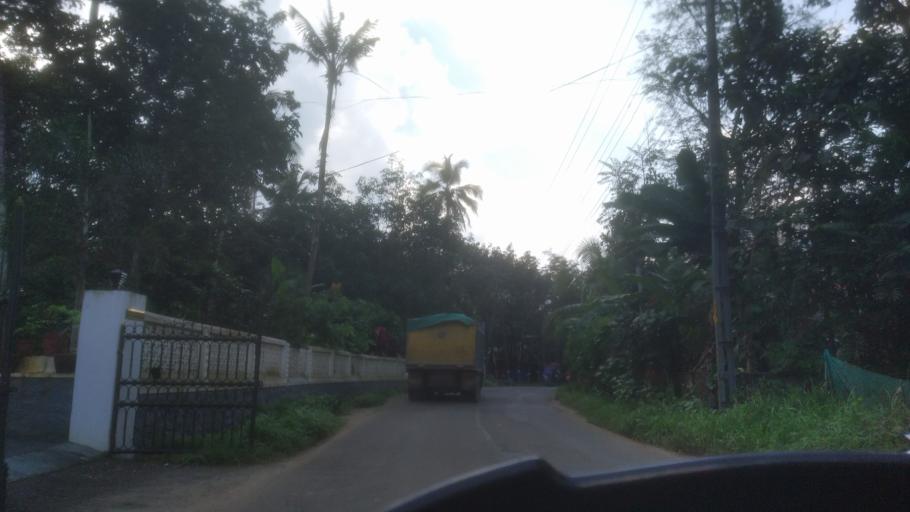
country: IN
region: Kerala
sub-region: Ernakulam
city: Kotamangalam
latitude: 10.0045
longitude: 76.6856
